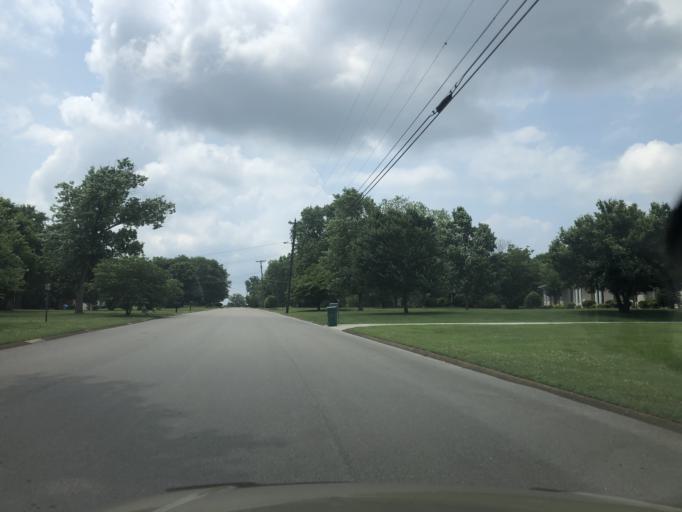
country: US
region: Tennessee
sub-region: Davidson County
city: Lakewood
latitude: 36.2402
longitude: -86.6221
